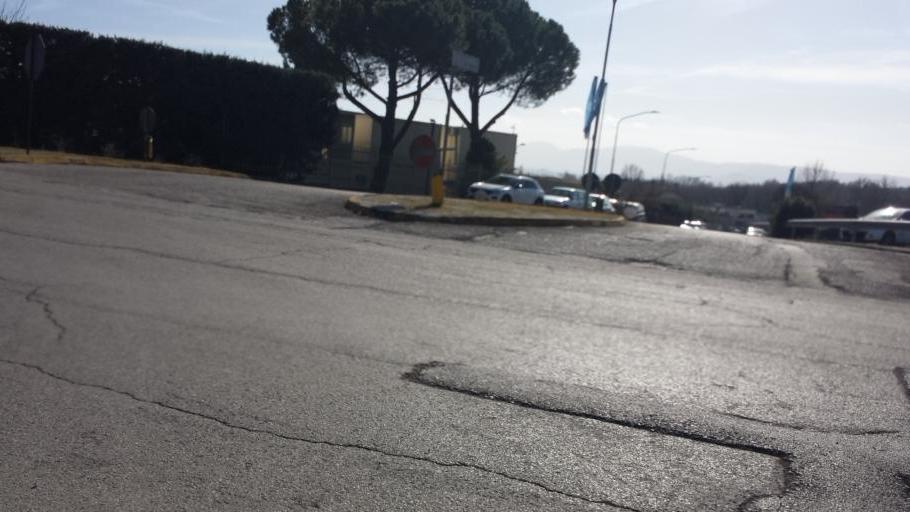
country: IT
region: Umbria
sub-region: Provincia di Terni
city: San Gemini
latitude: 42.5923
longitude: 12.5682
